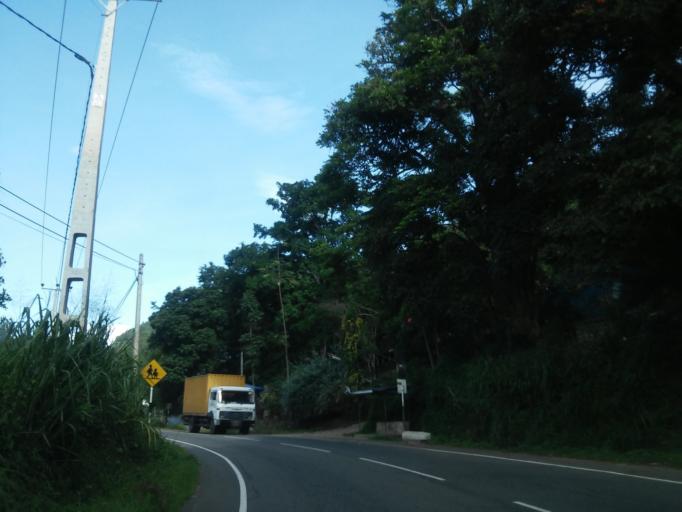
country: LK
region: Uva
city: Haputale
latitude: 6.7653
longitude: 80.8930
